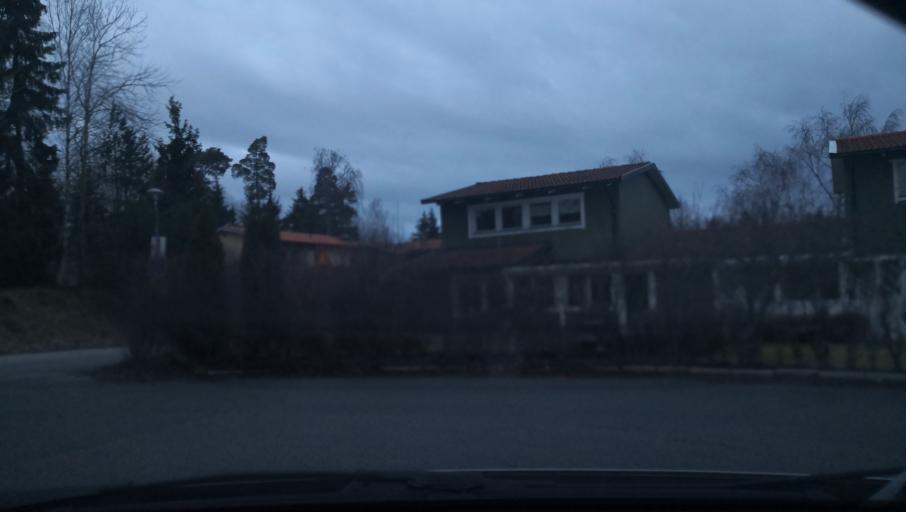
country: SE
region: Stockholm
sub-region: Taby Kommun
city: Taby
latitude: 59.4677
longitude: 18.0346
